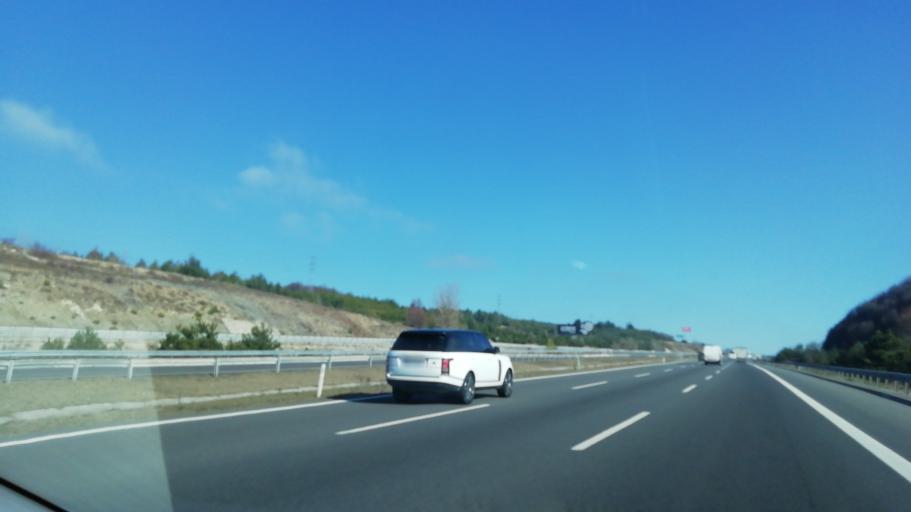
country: TR
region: Bolu
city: Yenicaga
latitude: 40.7492
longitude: 31.8965
